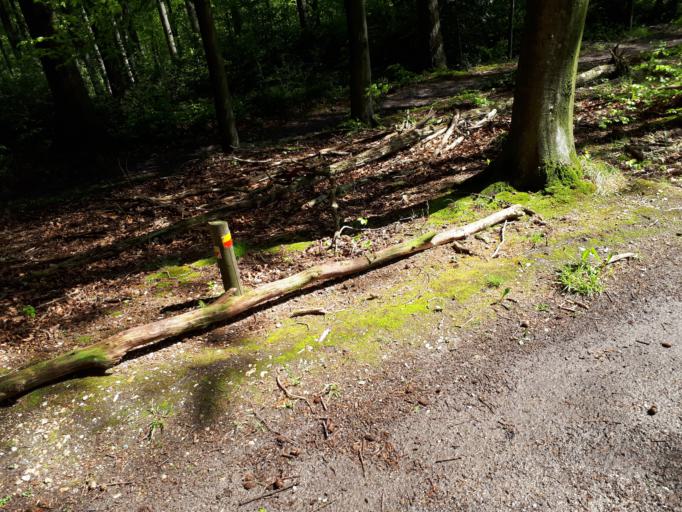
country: BE
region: Wallonia
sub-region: Province de Liege
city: Plombieres
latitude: 50.7602
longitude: 5.9806
